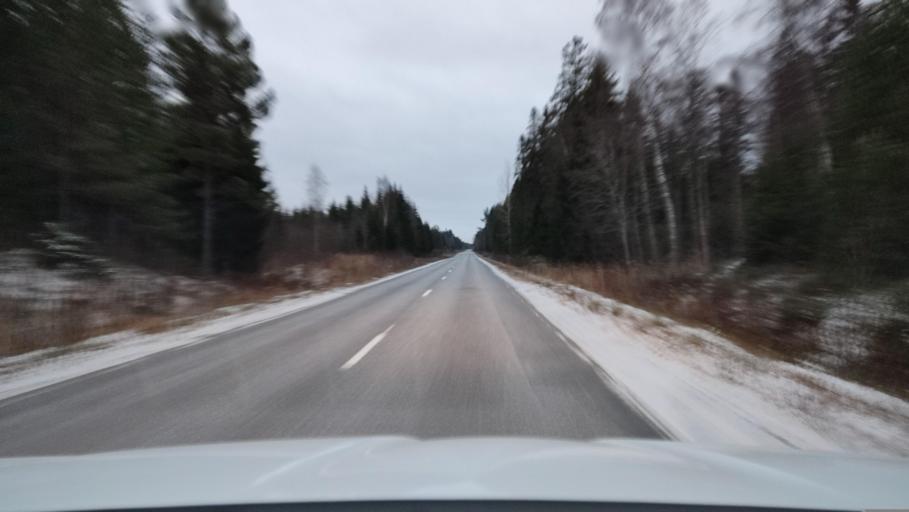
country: FI
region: Ostrobothnia
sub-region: Vaasa
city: Replot
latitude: 63.2567
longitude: 21.3670
